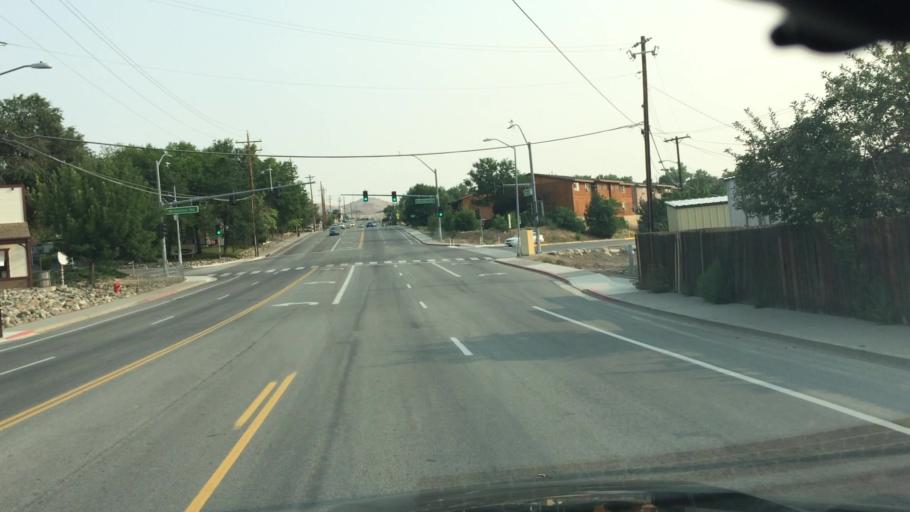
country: US
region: Nevada
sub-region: Washoe County
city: Reno
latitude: 39.5468
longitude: -119.7986
